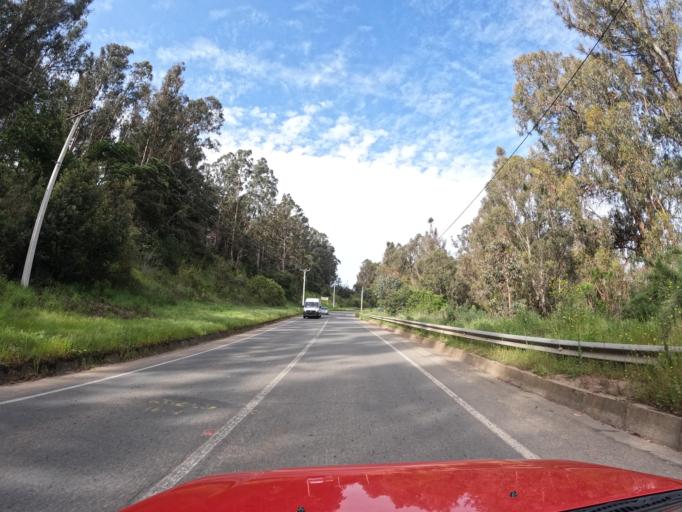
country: CL
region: O'Higgins
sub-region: Provincia de Colchagua
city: Santa Cruz
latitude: -34.3829
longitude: -71.9775
